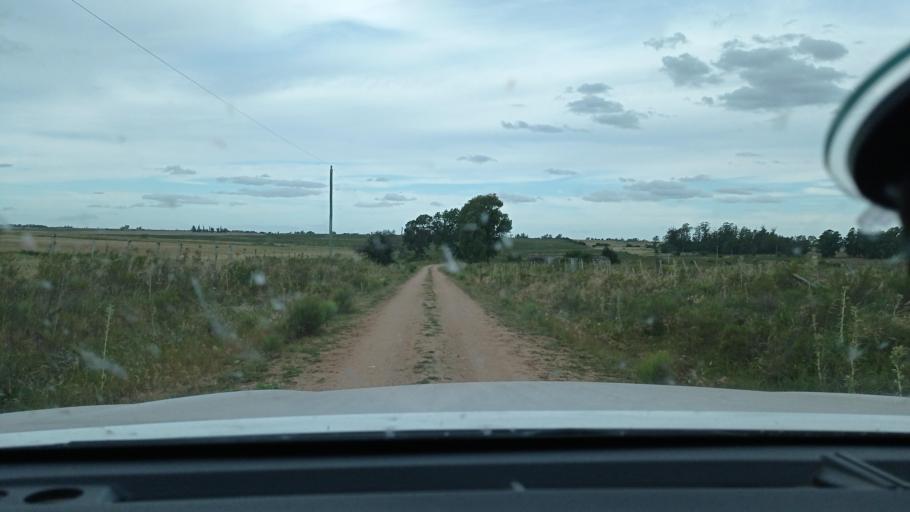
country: UY
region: Florida
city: Casupa
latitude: -34.1406
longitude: -55.8010
